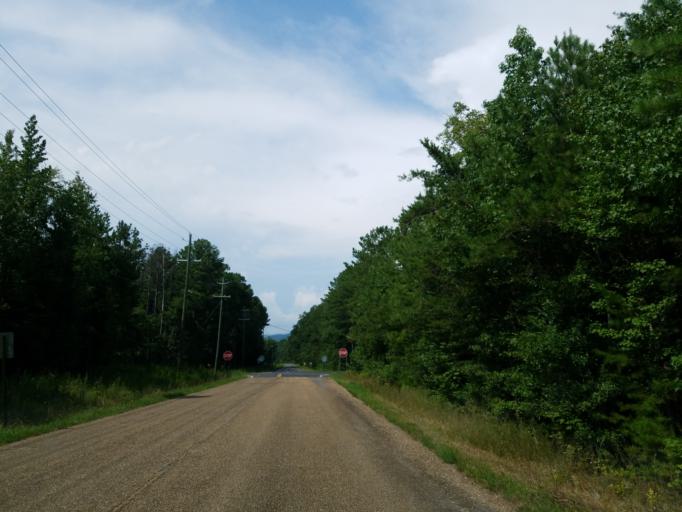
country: US
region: Georgia
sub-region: Murray County
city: Chatsworth
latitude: 34.5899
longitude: -84.6990
